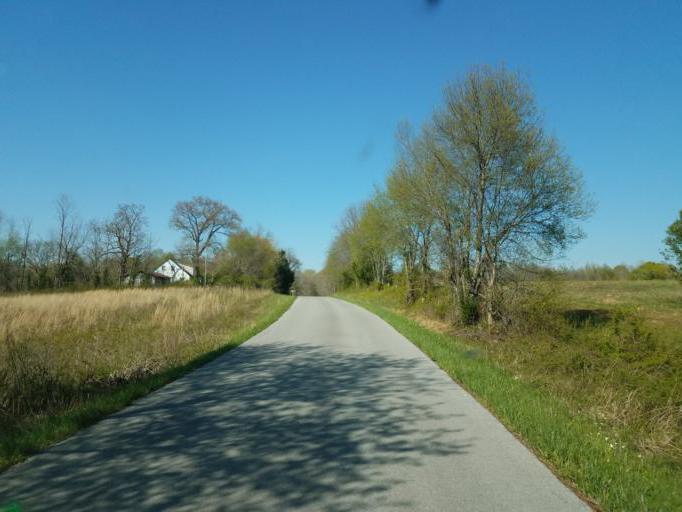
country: US
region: Kentucky
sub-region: Edmonson County
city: Brownsville
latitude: 37.1346
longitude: -86.1677
